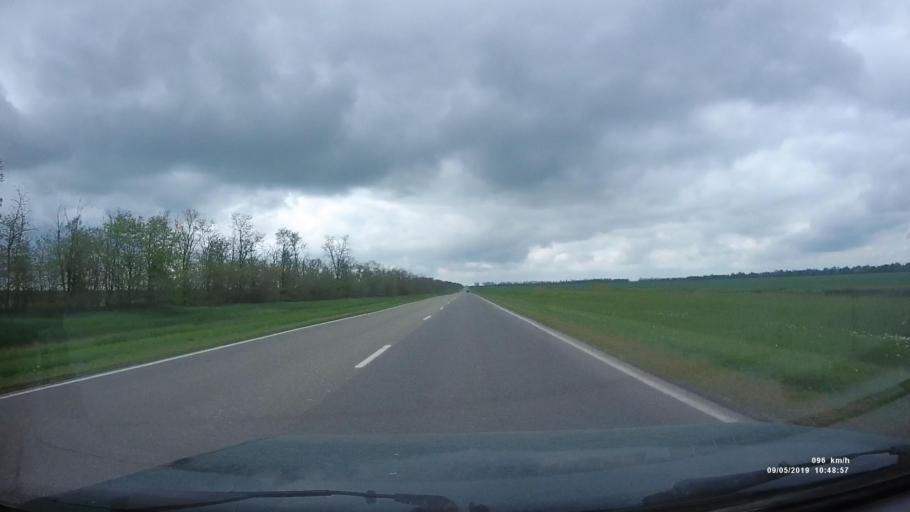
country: RU
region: Rostov
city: Peshkovo
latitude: 46.9493
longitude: 39.3555
